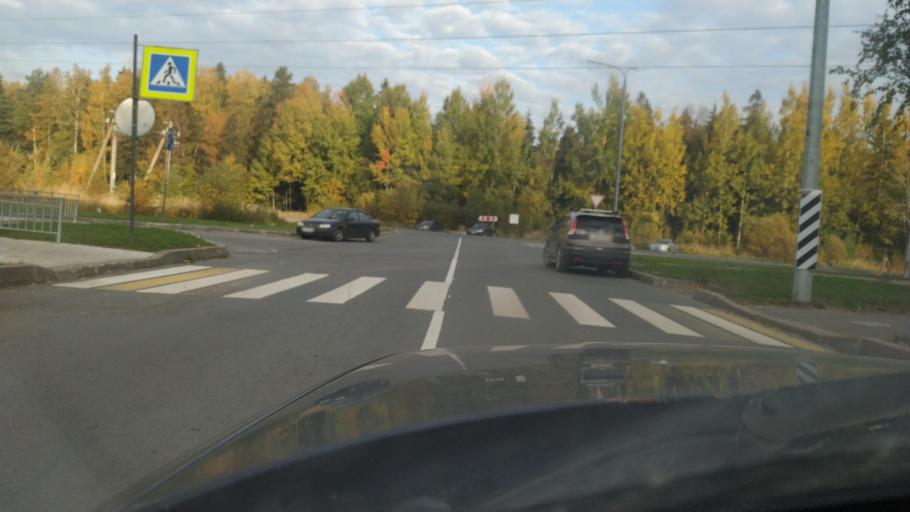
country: RU
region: Leningrad
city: Sosnovyy Bor
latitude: 59.9172
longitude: 29.0825
